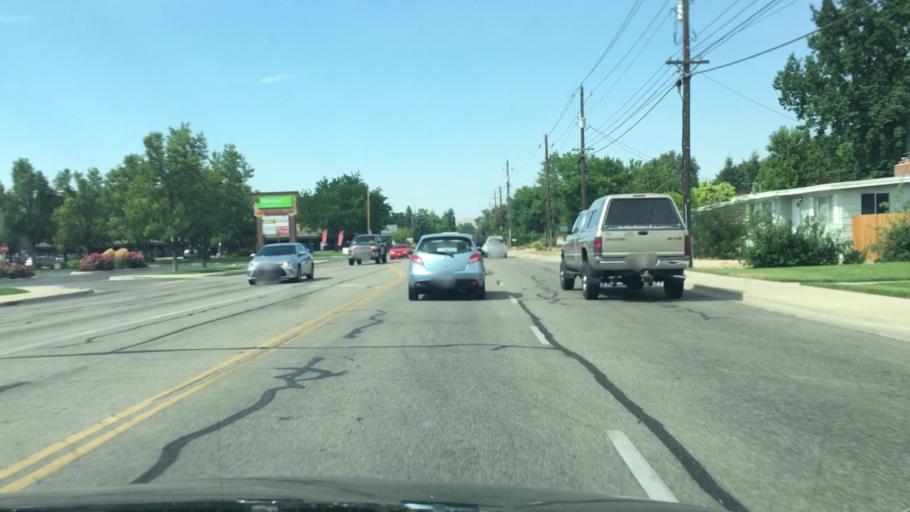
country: US
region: Idaho
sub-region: Ada County
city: Garden City
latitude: 43.6345
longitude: -116.2742
